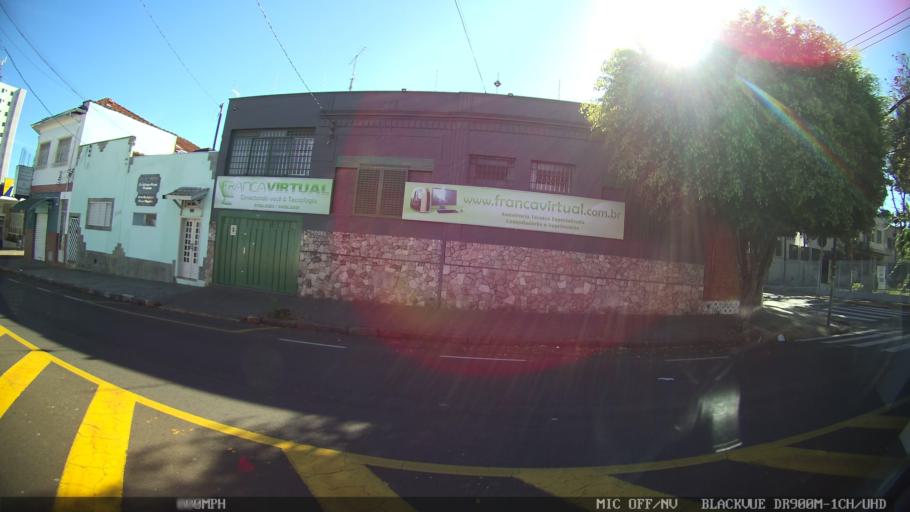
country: BR
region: Sao Paulo
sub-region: Franca
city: Franca
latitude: -20.5321
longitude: -47.3995
